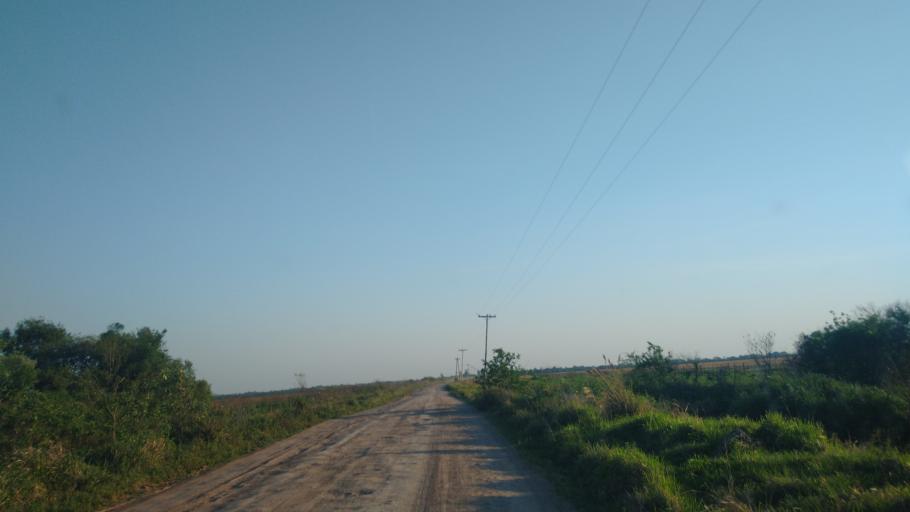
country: PY
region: Neembucu
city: Cerrito
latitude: -27.3910
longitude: -57.6585
